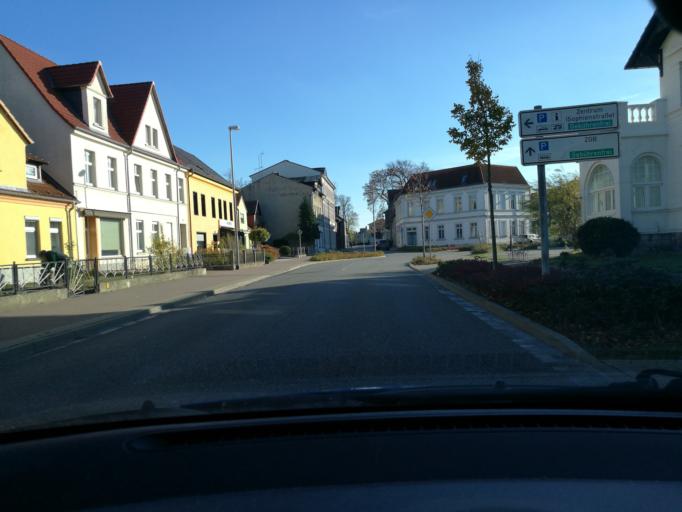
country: DE
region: Brandenburg
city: Perleberg
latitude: 53.0816
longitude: 11.8602
